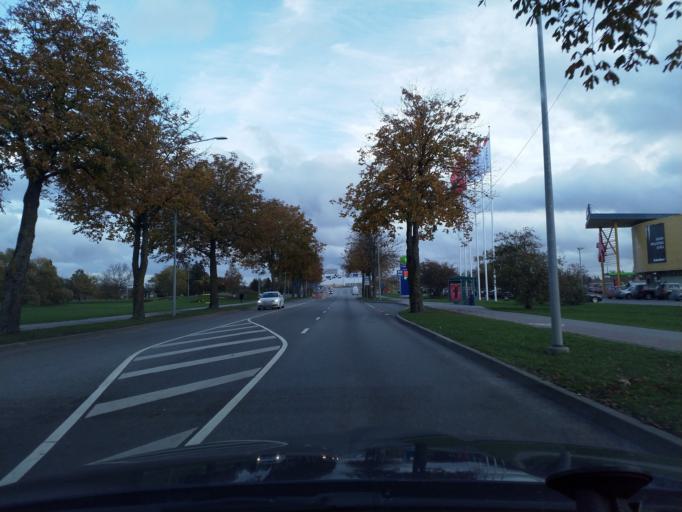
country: LV
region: Ventspils
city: Ventspils
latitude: 57.3885
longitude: 21.5796
